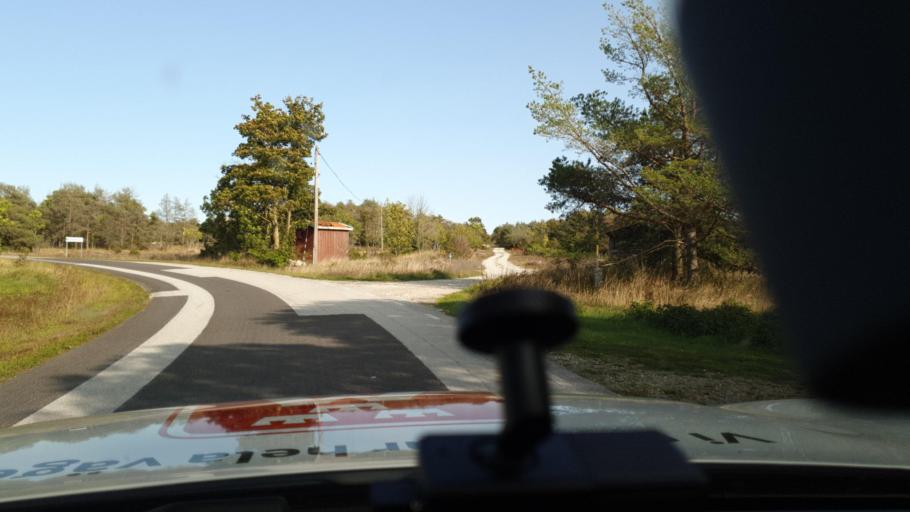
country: SE
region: Gotland
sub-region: Gotland
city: Slite
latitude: 57.6797
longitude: 18.6364
